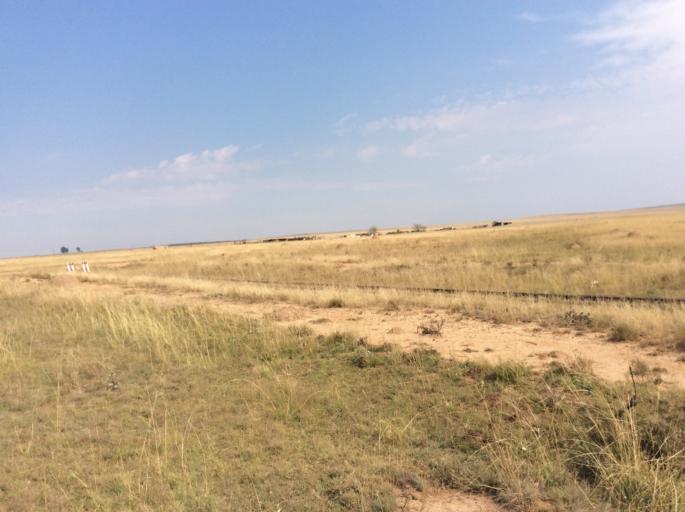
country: LS
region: Mafeteng
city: Mafeteng
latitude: -29.7315
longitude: 27.0218
